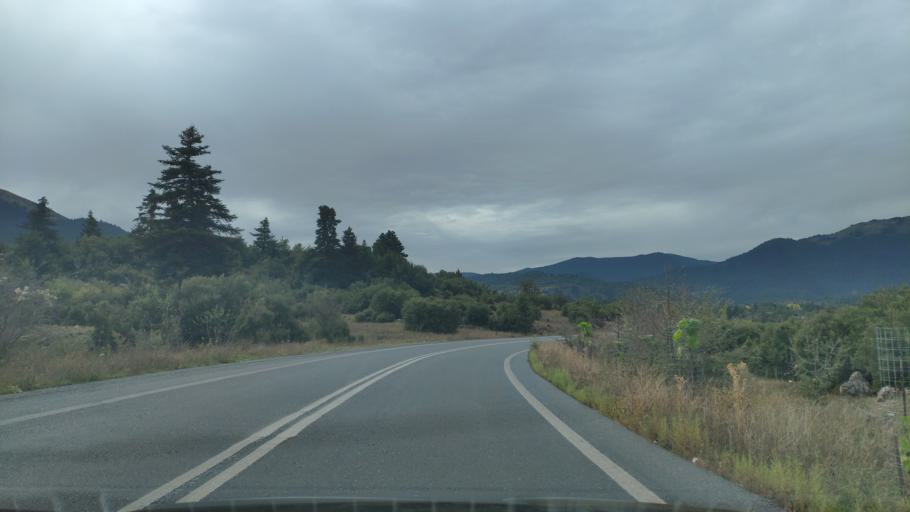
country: GR
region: Peloponnese
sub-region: Nomos Arkadias
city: Dimitsana
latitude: 37.6594
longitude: 22.1904
